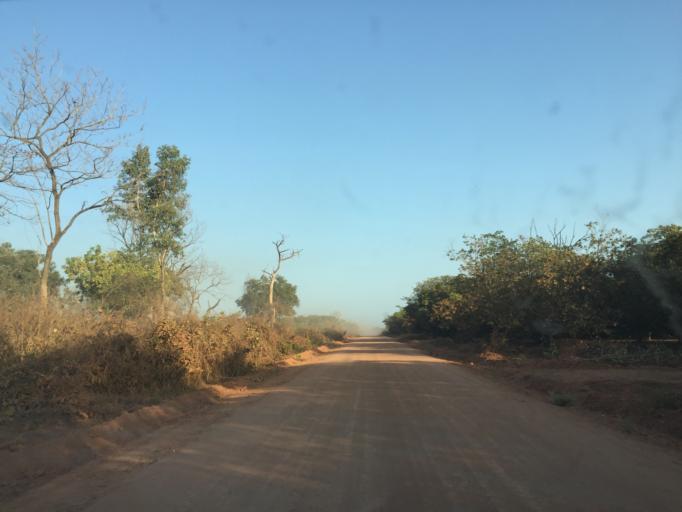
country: GW
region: Oio
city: Farim
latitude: 12.5304
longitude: -15.2716
